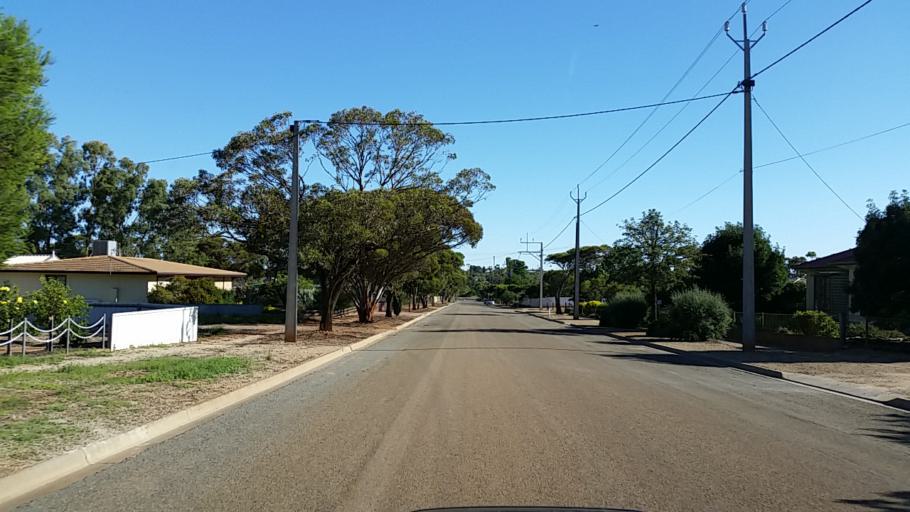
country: AU
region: South Australia
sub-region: Peterborough
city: Peterborough
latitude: -32.9679
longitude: 138.8317
